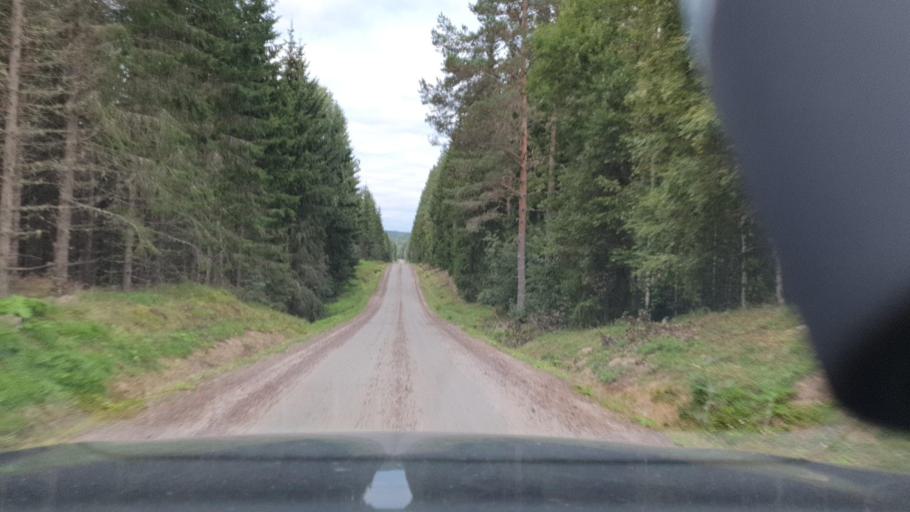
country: SE
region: Vaermland
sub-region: Munkfors Kommun
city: Munkfors
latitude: 59.8929
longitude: 13.5061
